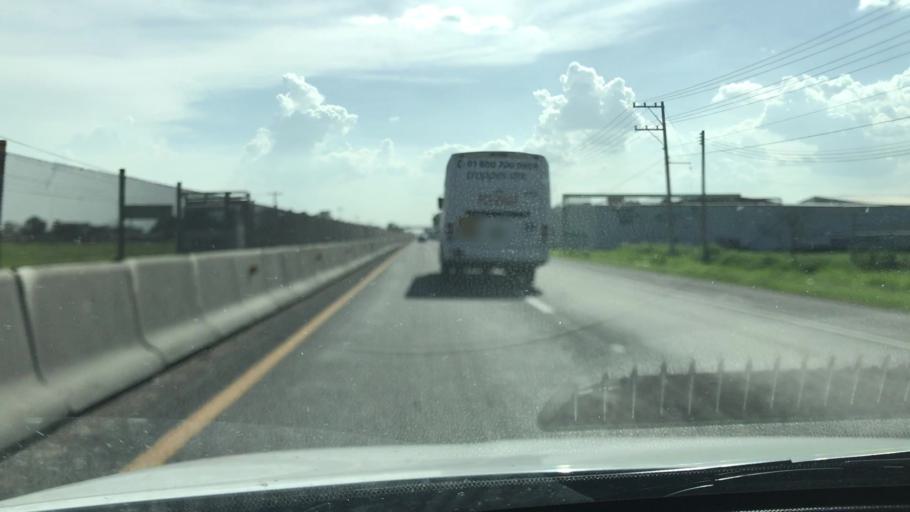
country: MX
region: Guanajuato
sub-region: Villagran
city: El Chinaco (El Pujido)
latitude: 20.5138
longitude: -100.9168
